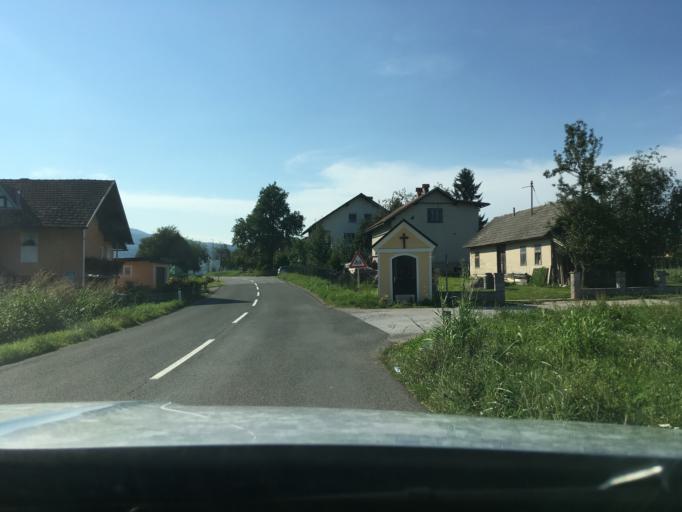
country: SI
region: Crnomelj
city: Crnomelj
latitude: 45.5184
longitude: 15.1776
